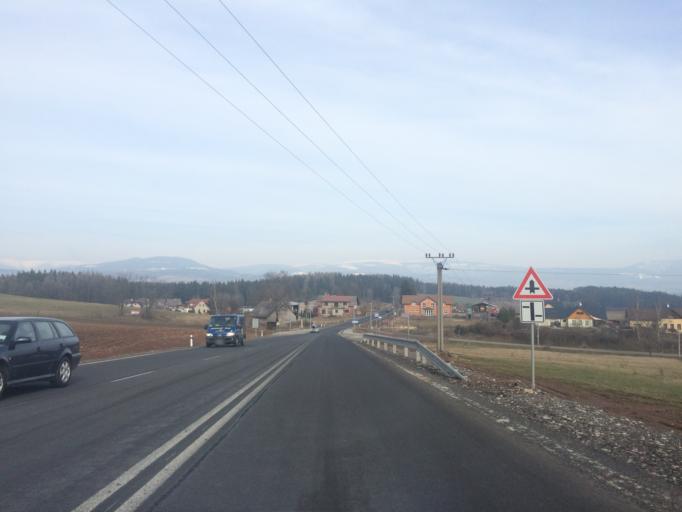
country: CZ
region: Liberecky
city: Studenec
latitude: 50.5718
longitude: 15.5564
